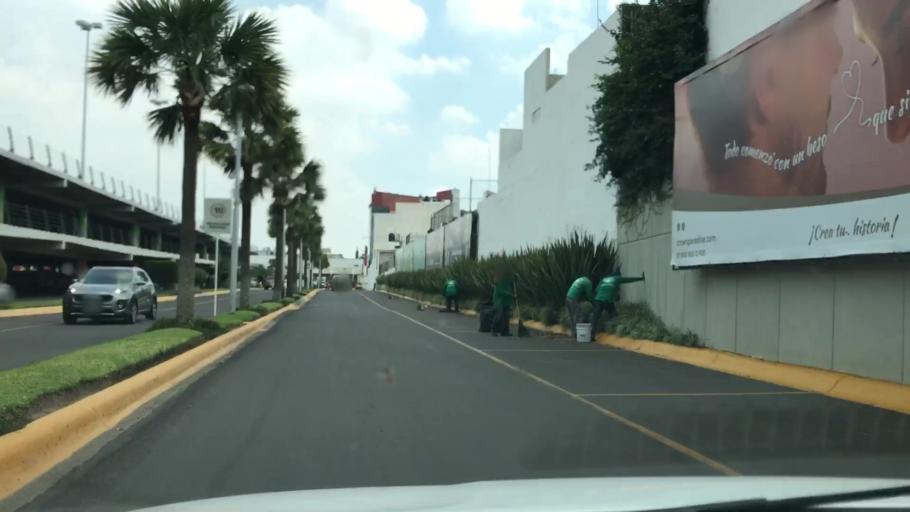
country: MX
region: Jalisco
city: Guadalajara
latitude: 20.6755
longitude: -103.4316
